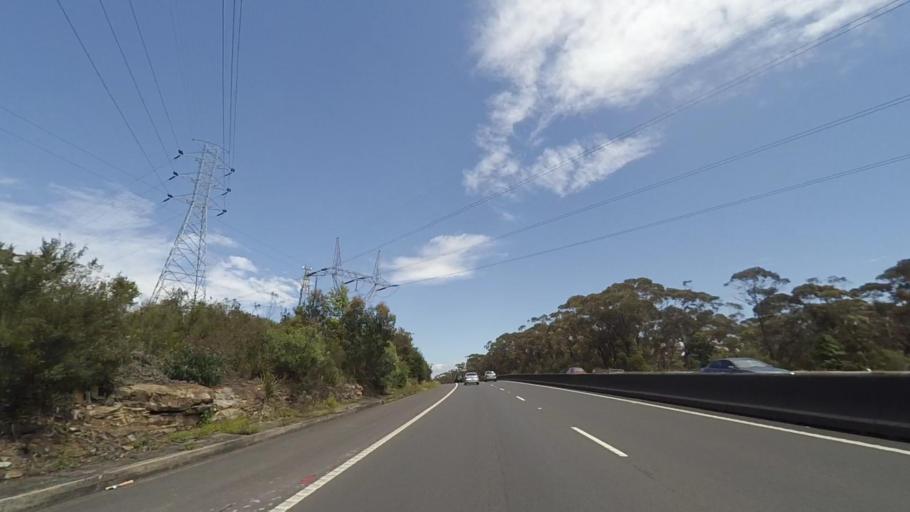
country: AU
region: New South Wales
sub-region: Wollongong
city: Bulli
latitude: -34.3224
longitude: 150.8828
